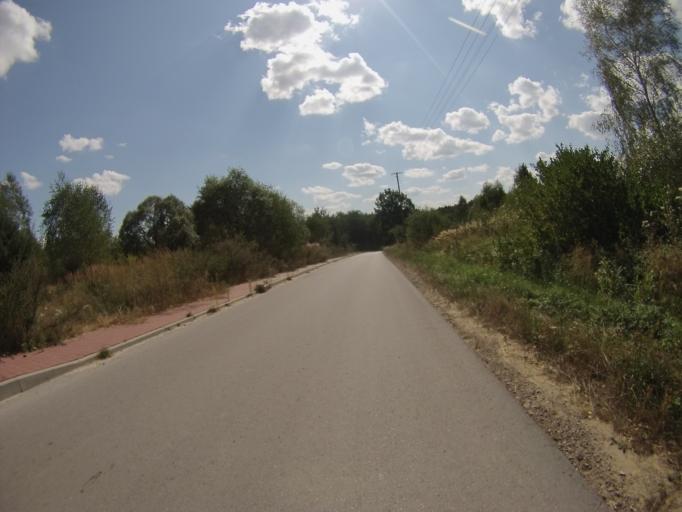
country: PL
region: Swietokrzyskie
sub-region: Powiat kielecki
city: Rakow
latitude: 50.7041
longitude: 21.0538
